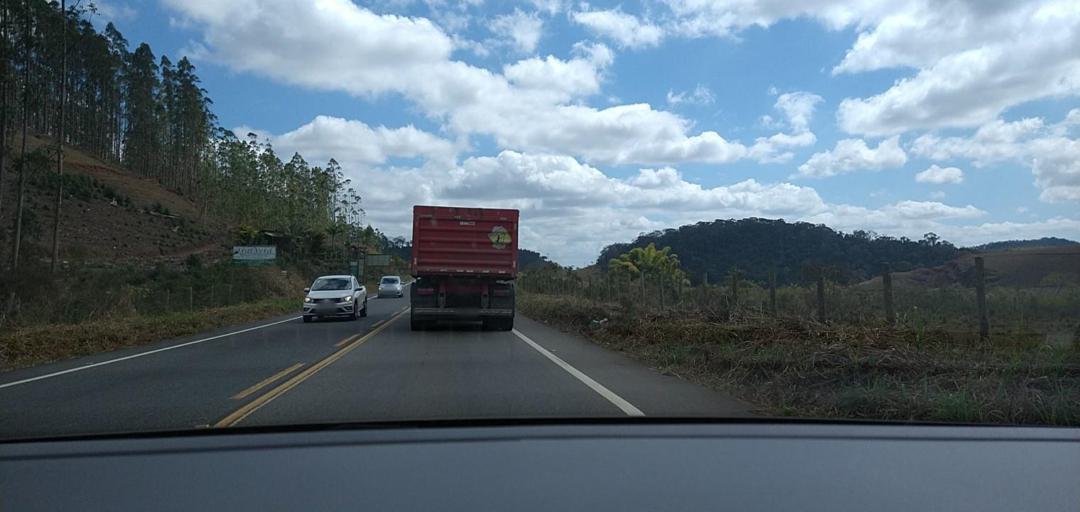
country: BR
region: Minas Gerais
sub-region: Ponte Nova
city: Ponte Nova
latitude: -20.4798
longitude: -42.8808
